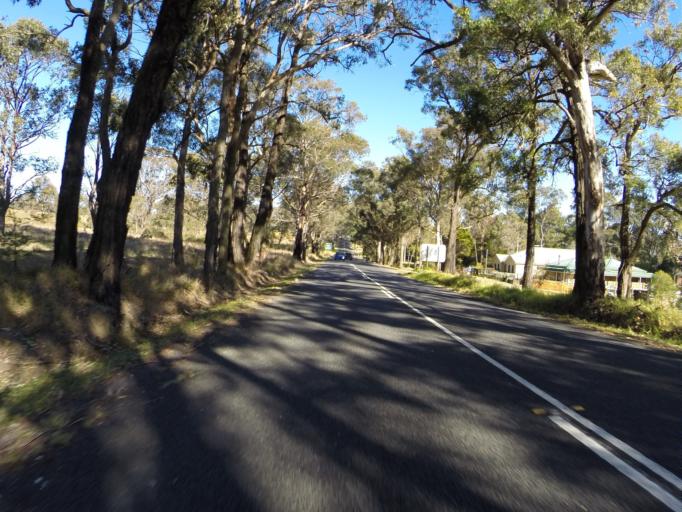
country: AU
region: New South Wales
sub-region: Wollondilly
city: Douglas Park
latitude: -34.2348
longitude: 150.7327
